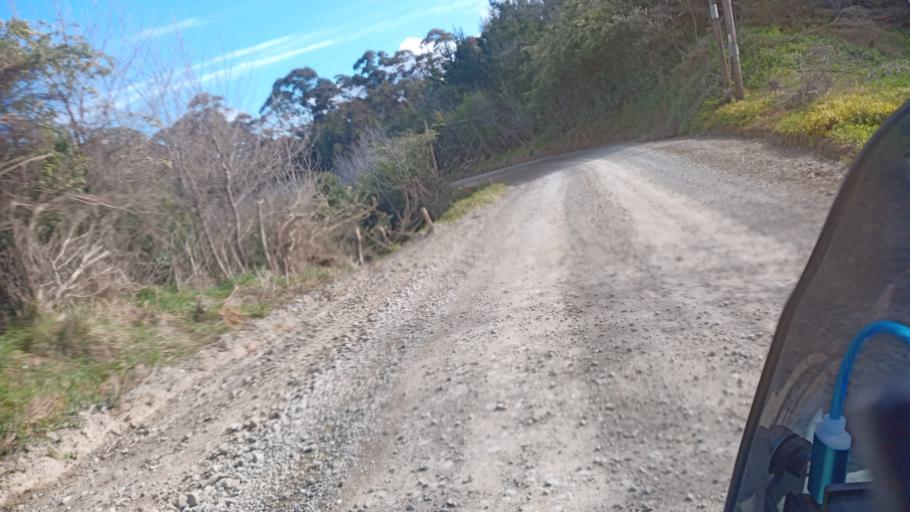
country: NZ
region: Gisborne
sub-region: Gisborne District
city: Gisborne
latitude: -38.1346
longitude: 178.1912
